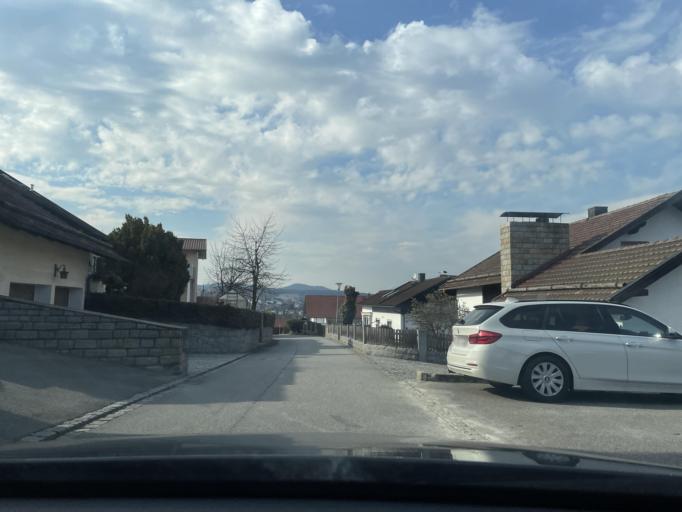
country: DE
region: Bavaria
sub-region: Lower Bavaria
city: Viechtach
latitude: 49.0824
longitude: 12.8954
